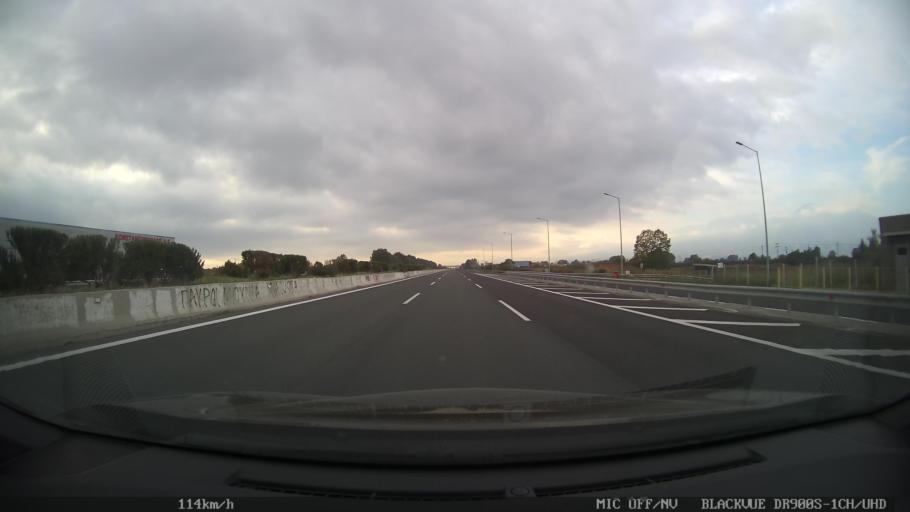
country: GR
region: Central Macedonia
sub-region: Nomos Pierias
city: Peristasi
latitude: 40.2364
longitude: 22.5369
